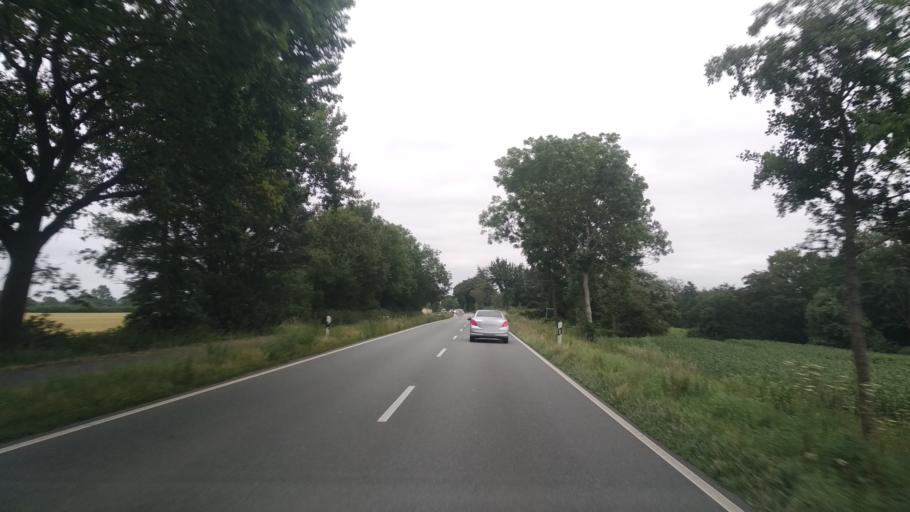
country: DE
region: Schleswig-Holstein
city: Langballig
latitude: 54.8006
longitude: 9.6194
